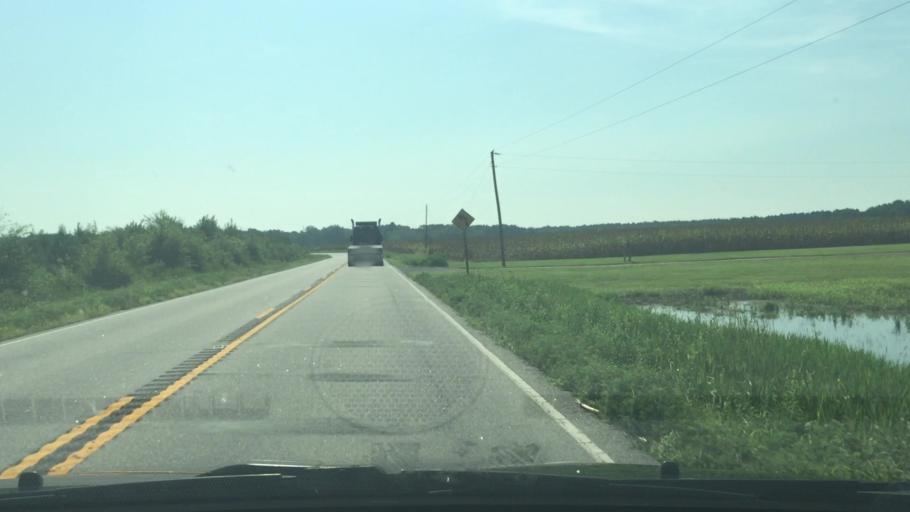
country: US
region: Virginia
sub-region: Sussex County
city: Sussex
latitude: 36.9782
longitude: -77.2288
